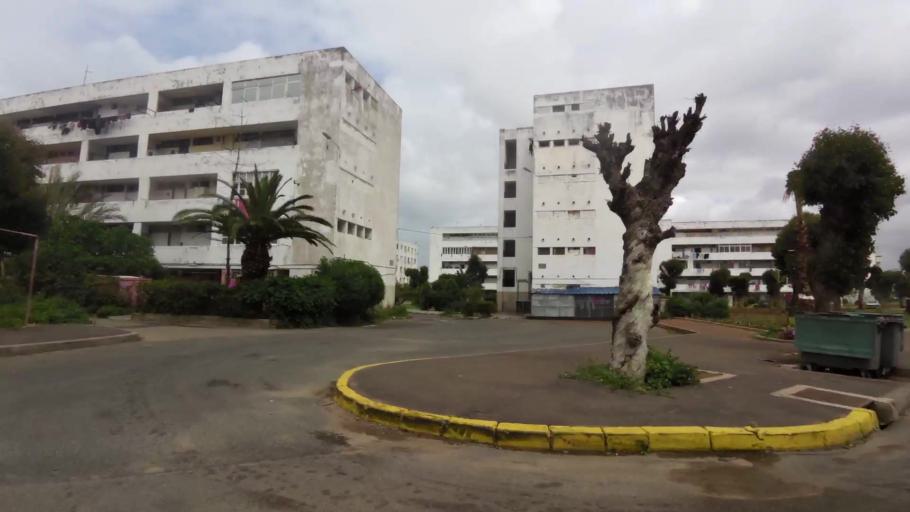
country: MA
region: Grand Casablanca
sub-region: Casablanca
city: Casablanca
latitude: 33.6019
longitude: -7.6531
